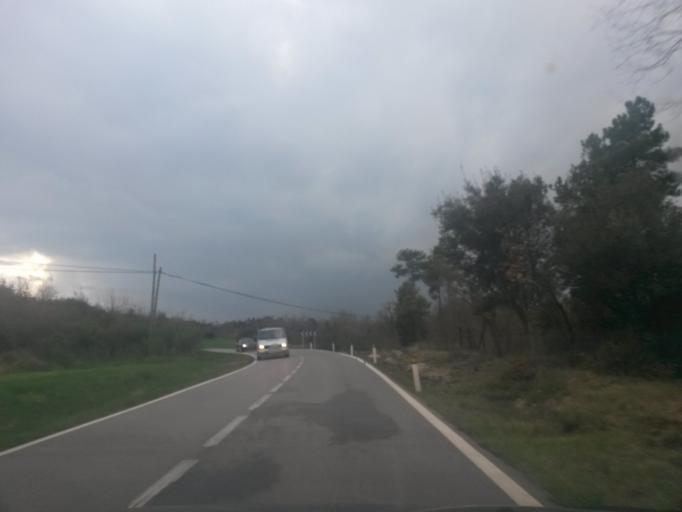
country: ES
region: Catalonia
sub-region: Provincia de Barcelona
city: Sagas
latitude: 42.0331
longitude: 1.9837
